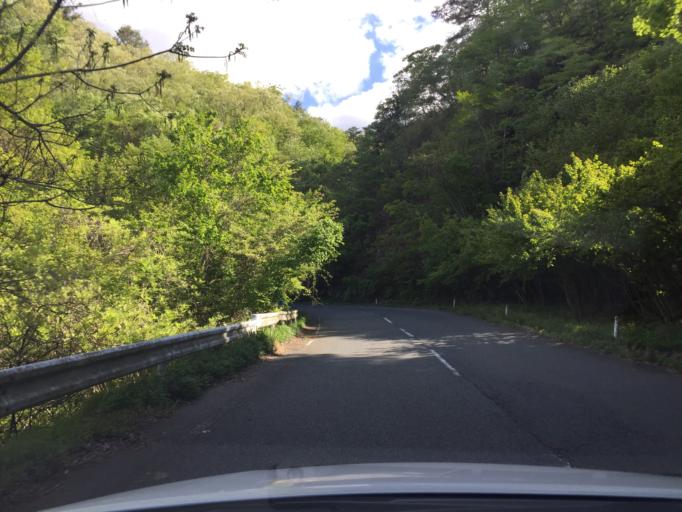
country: JP
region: Miyagi
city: Marumori
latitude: 37.7291
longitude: 140.8027
